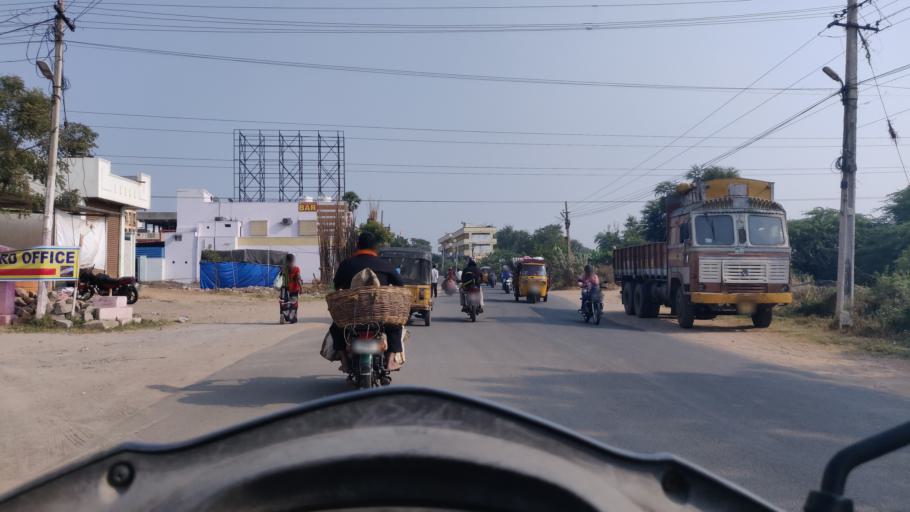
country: IN
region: Telangana
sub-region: Rangareddi
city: Uppal Kalan
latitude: 17.3997
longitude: 78.5845
